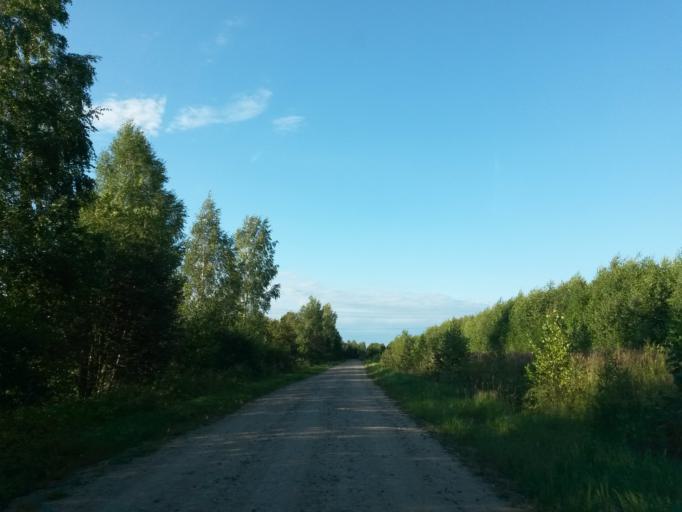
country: RU
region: Jaroslavl
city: Tutayev
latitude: 57.9408
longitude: 39.4462
